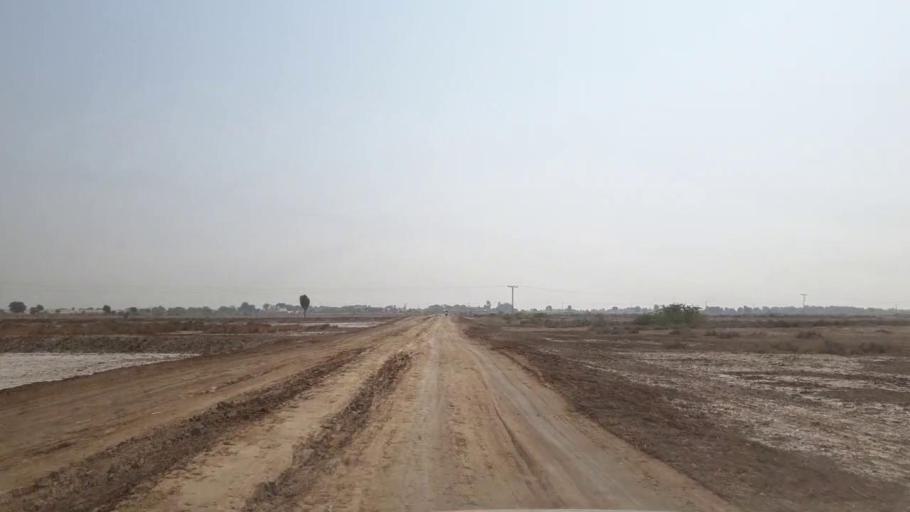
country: PK
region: Sindh
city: Mirpur Khas
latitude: 25.6435
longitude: 69.1426
